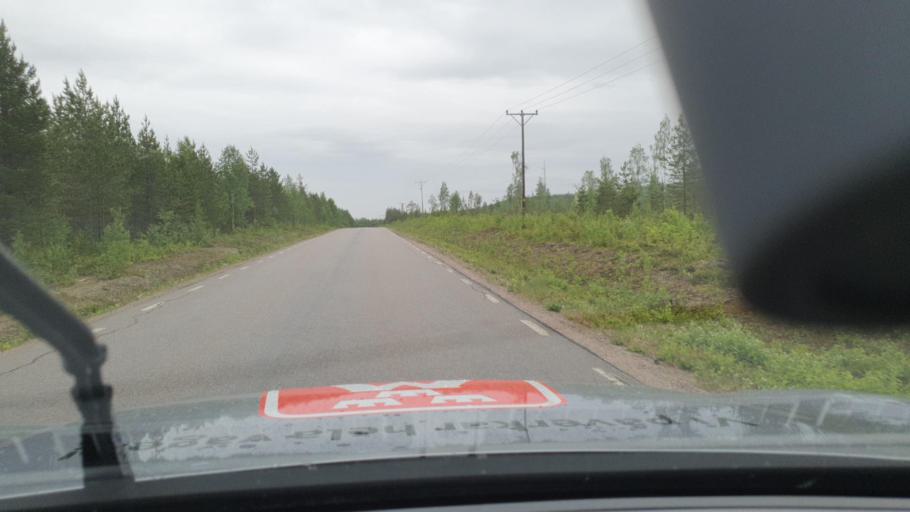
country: SE
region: Norrbotten
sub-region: Pajala Kommun
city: Pajala
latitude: 66.7583
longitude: 23.1563
